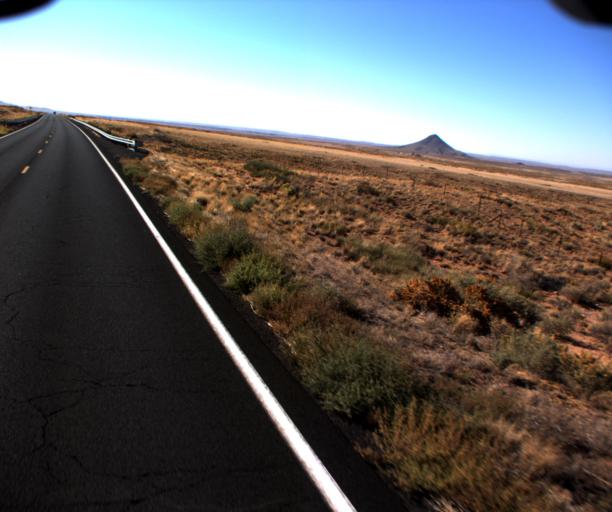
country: US
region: Arizona
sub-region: Navajo County
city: Dilkon
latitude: 35.4172
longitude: -110.4268
